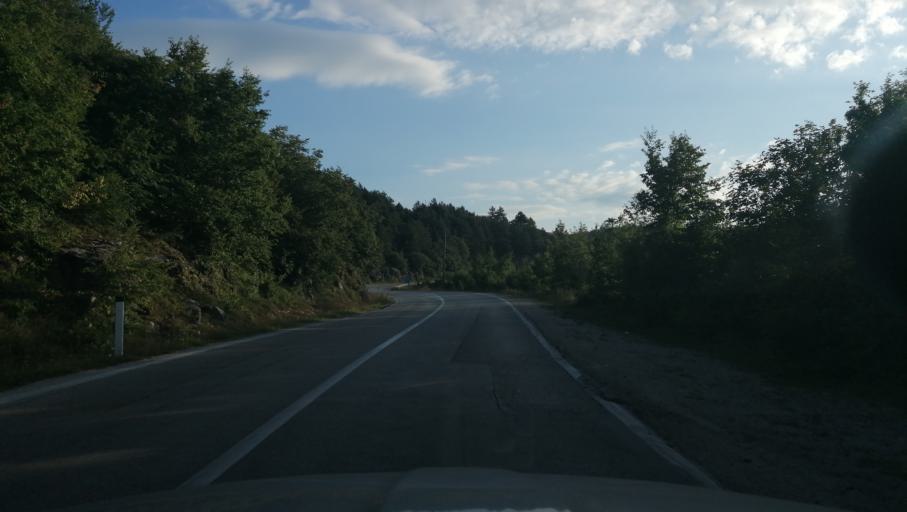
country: BA
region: Federation of Bosnia and Herzegovina
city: Prozor
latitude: 43.8412
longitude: 17.5920
